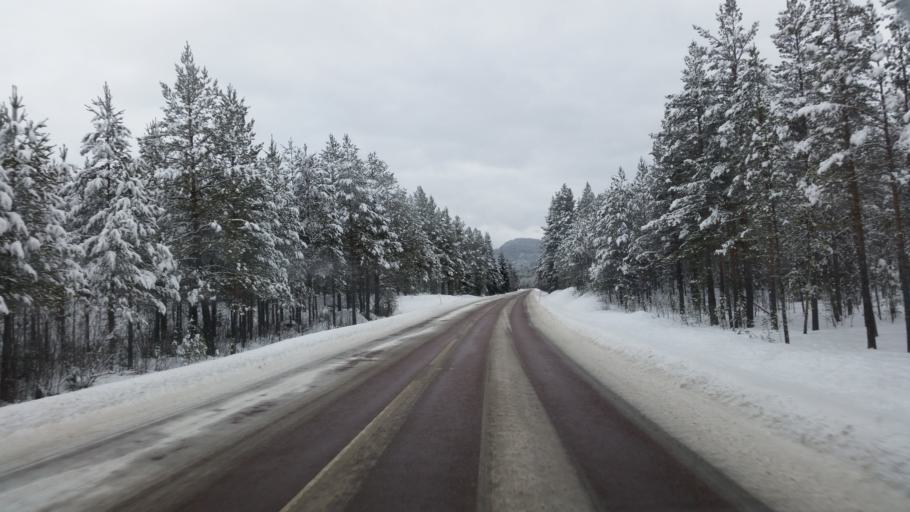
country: SE
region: Jaemtland
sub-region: Harjedalens Kommun
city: Sveg
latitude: 62.3782
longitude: 14.6722
